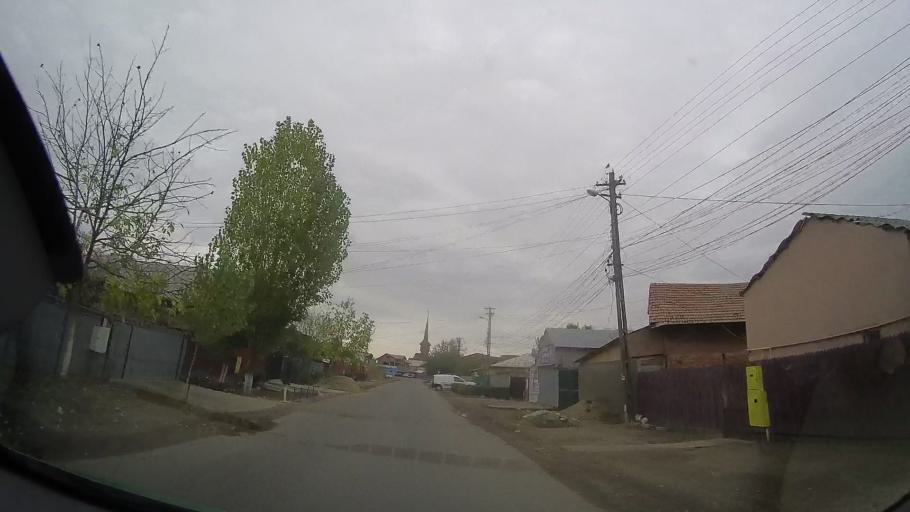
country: RO
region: Prahova
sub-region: Oras Mizil
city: Mizil
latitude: 45.0012
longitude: 26.4326
